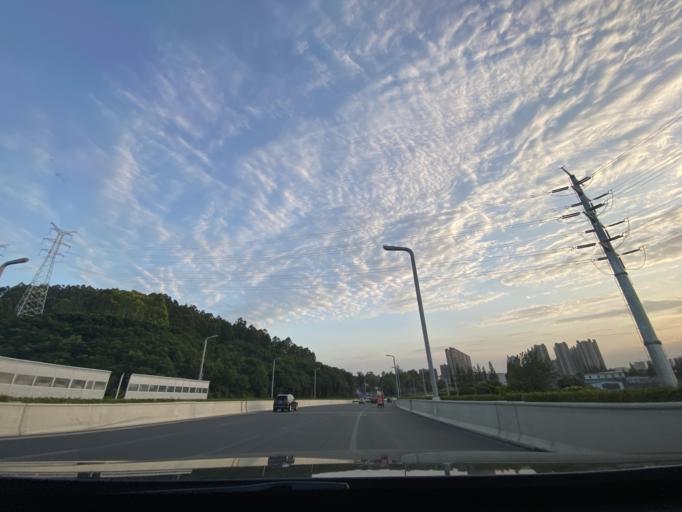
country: CN
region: Sichuan
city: Longquan
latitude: 30.5899
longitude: 104.3024
